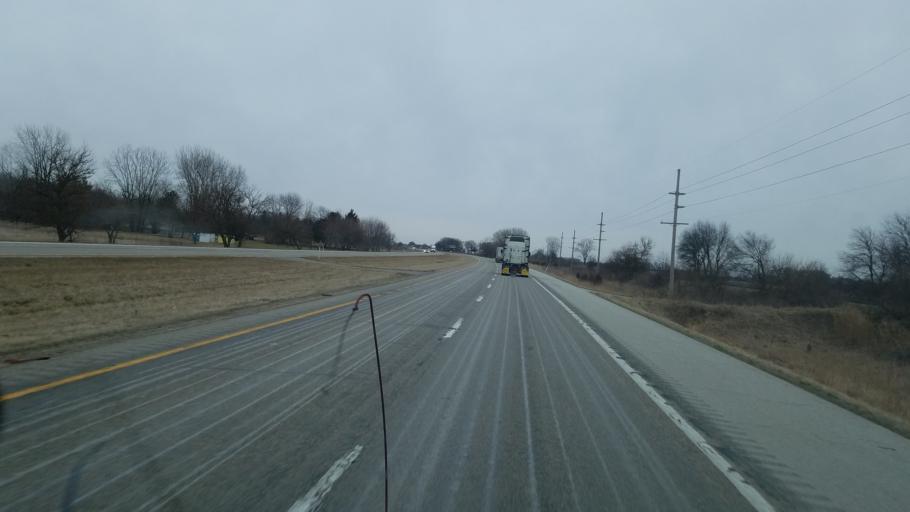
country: US
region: Indiana
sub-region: LaPorte County
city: Kingsford Heights
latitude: 41.3944
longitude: -86.6628
